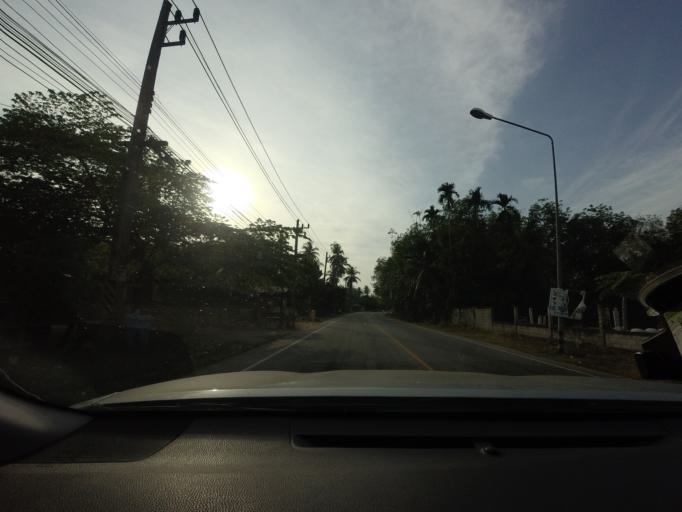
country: TH
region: Narathiwat
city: Ra-ngae
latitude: 6.3393
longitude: 101.7080
